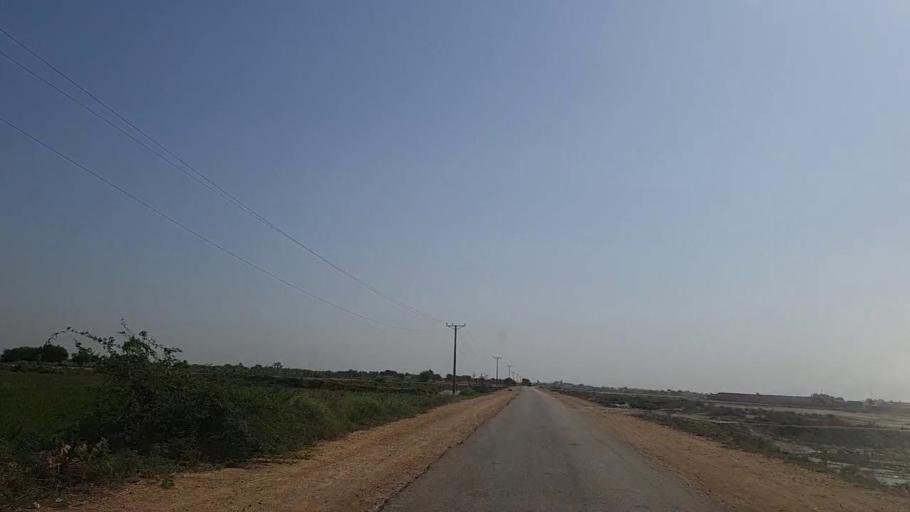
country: PK
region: Sindh
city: Mirpur Batoro
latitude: 24.6320
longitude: 68.2928
